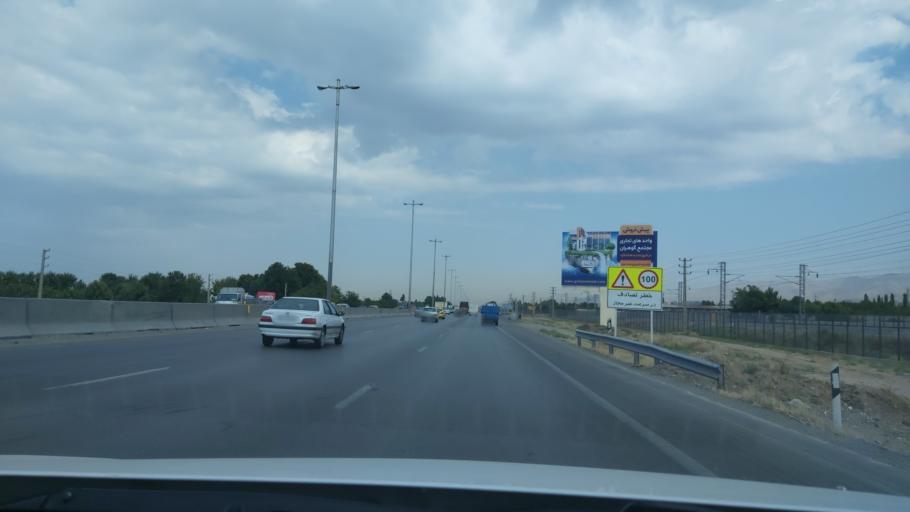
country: IR
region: Alborz
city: Hashtgerd
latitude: 35.9323
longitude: 50.7608
